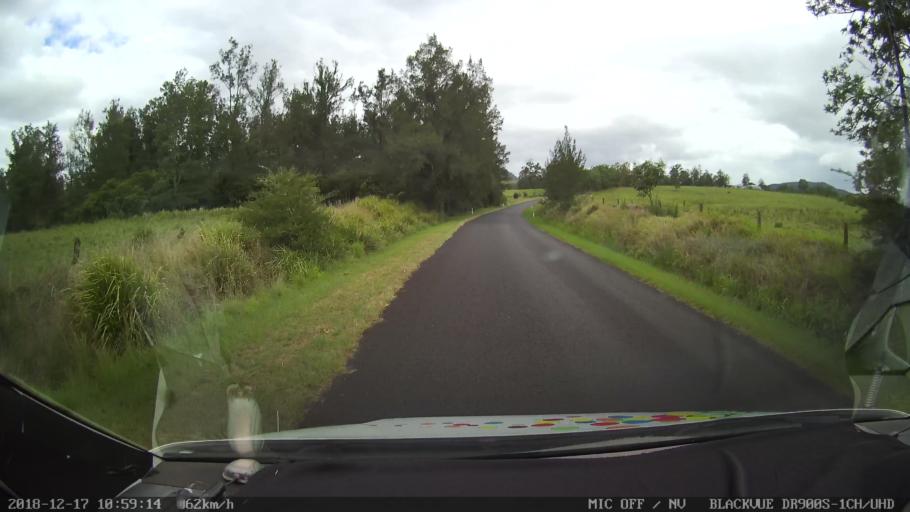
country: AU
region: New South Wales
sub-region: Richmond Valley
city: Casino
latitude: -28.8220
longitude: 152.6099
